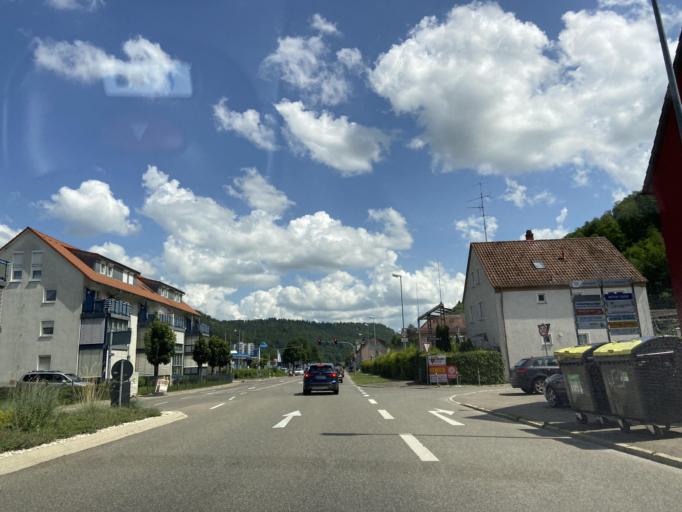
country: DE
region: Baden-Wuerttemberg
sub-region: Tuebingen Region
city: Albstadt
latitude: 48.2061
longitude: 9.0351
